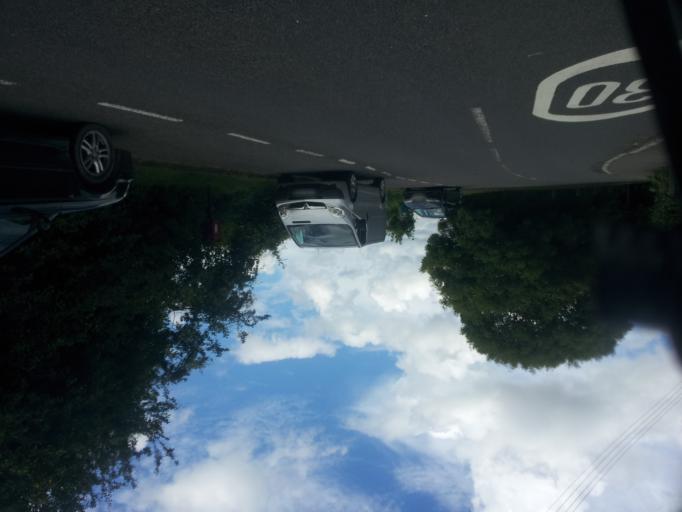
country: GB
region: England
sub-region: Kent
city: Kings Hill
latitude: 51.2580
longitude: 0.3749
